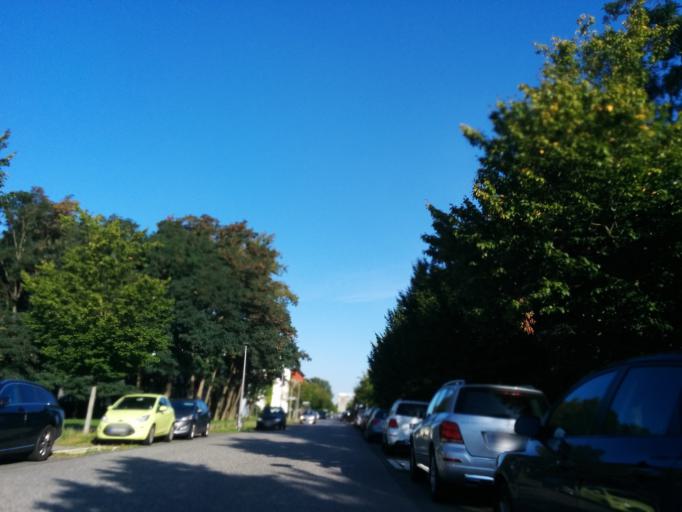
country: DE
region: Berlin
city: Adlershof
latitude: 52.4273
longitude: 13.5403
